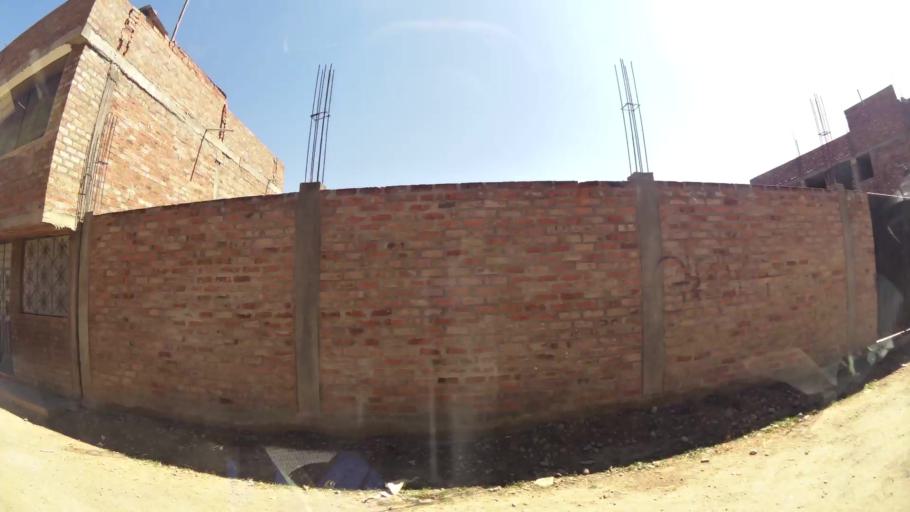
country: PE
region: Junin
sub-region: Provincia de Concepcion
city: Concepcion
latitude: -11.9159
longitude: -75.3205
